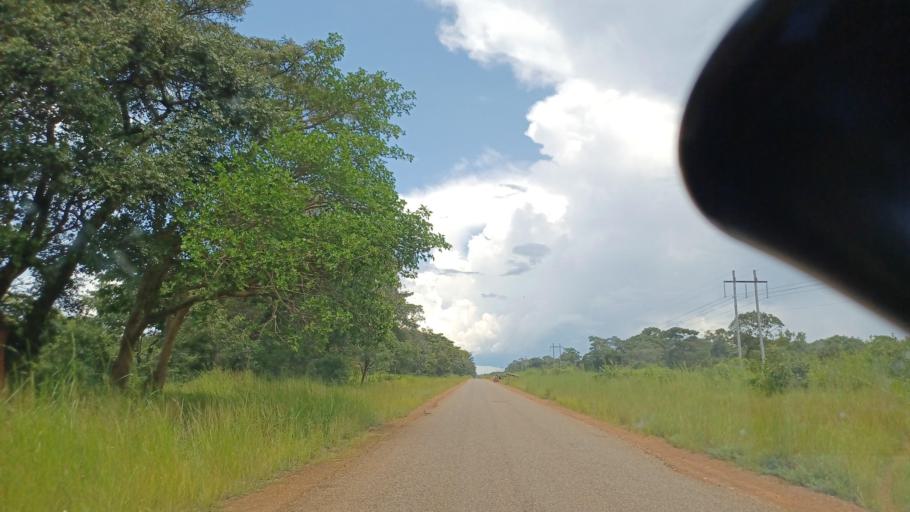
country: ZM
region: North-Western
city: Kasempa
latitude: -12.8731
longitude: 26.0419
